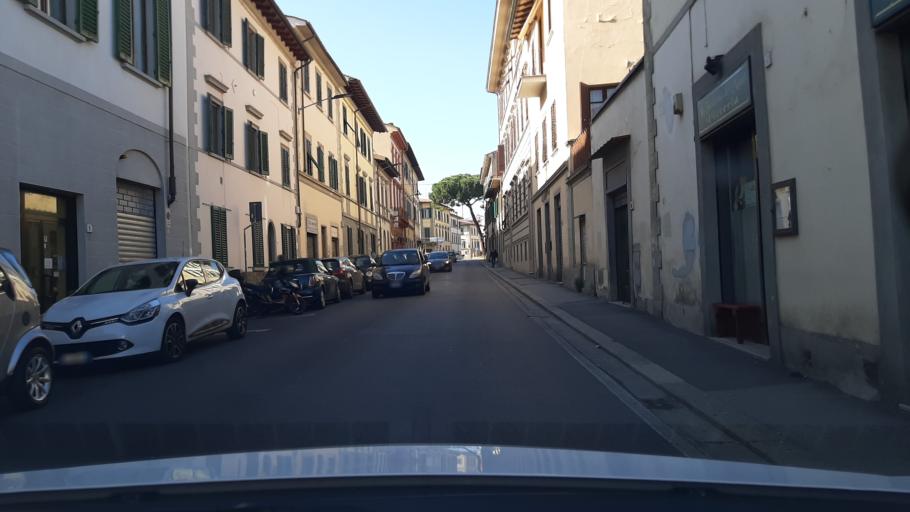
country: IT
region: Tuscany
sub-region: Province of Florence
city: Fiesole
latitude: 43.7722
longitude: 11.2859
